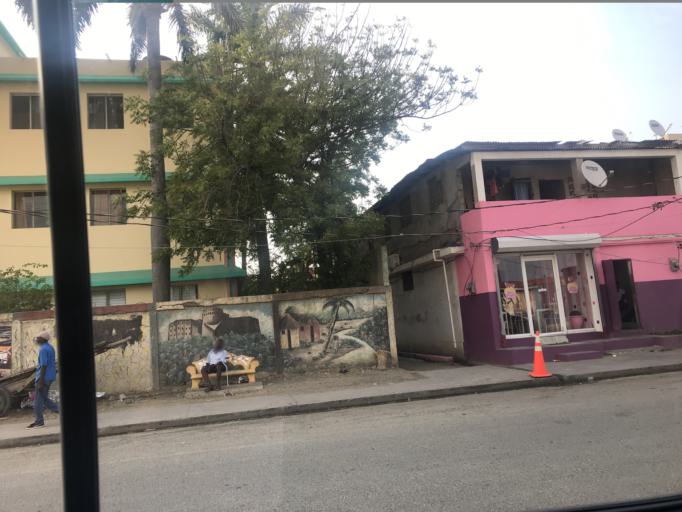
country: HT
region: Nord
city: Okap
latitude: 19.7614
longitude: -72.1966
